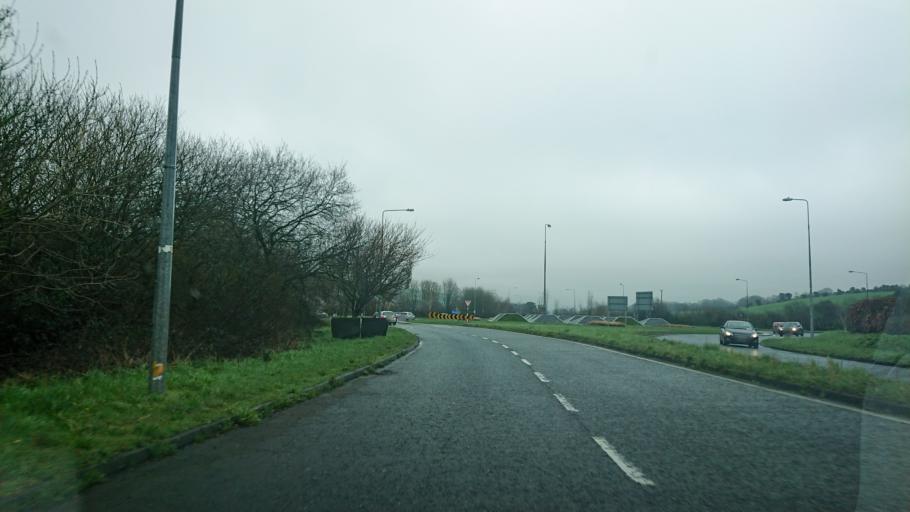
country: IE
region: Munster
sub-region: County Cork
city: Killumney
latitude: 51.8016
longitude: -8.5752
